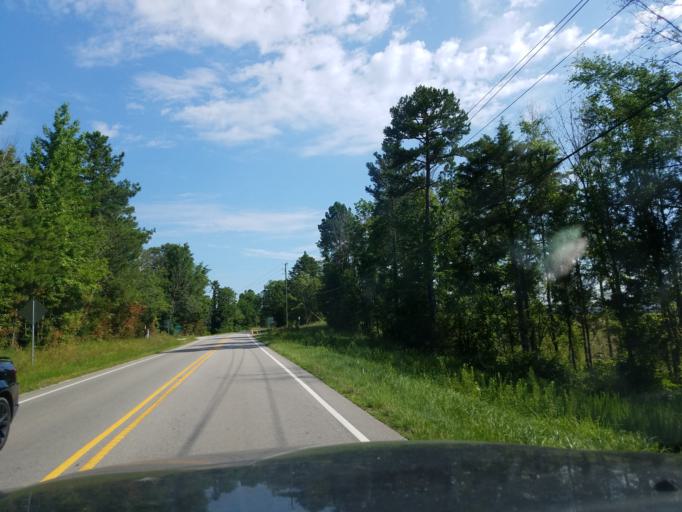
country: US
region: North Carolina
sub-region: Vance County
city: Henderson
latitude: 36.3684
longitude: -78.4190
